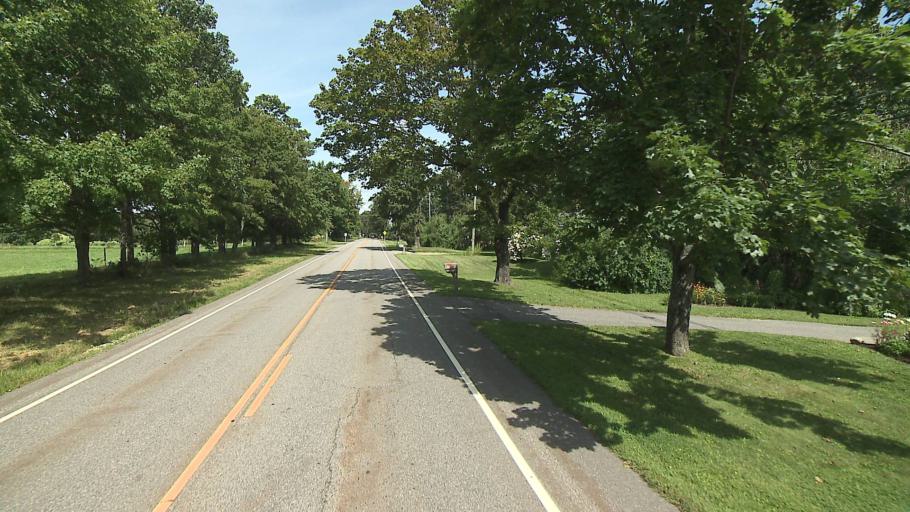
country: US
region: Connecticut
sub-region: Litchfield County
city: Bethlehem Village
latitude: 41.6798
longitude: -73.1980
